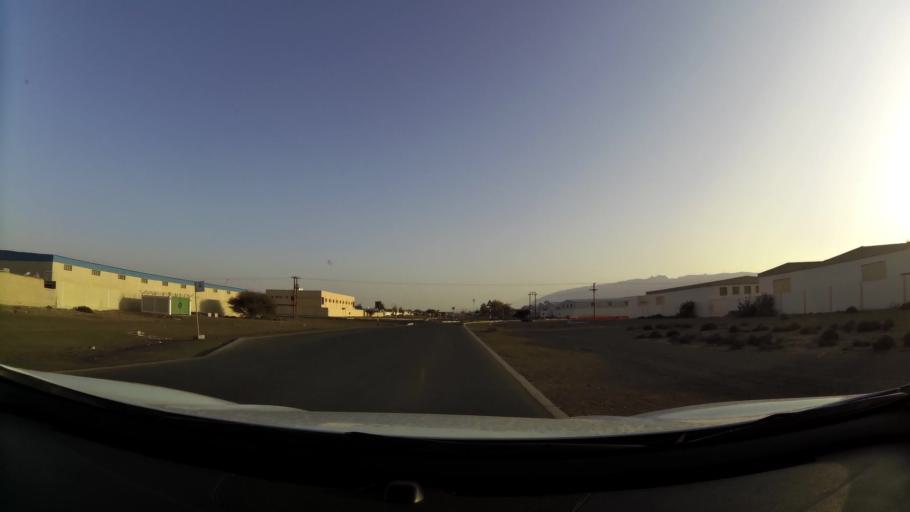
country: AE
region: Abu Dhabi
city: Al Ain
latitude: 24.1508
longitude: 55.8193
